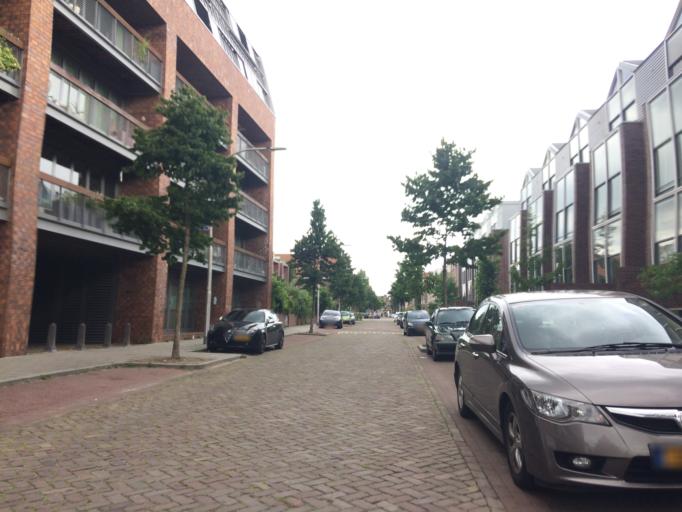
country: NL
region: Gelderland
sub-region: Gemeente Nijmegen
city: Nijmegen
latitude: 51.8385
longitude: 5.8541
